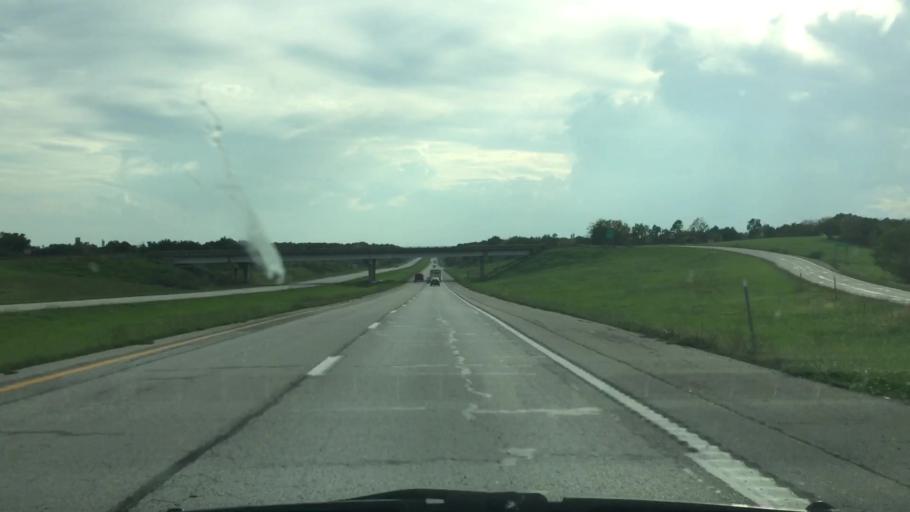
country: US
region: Missouri
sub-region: Harrison County
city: Bethany
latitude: 40.1067
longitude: -94.0698
